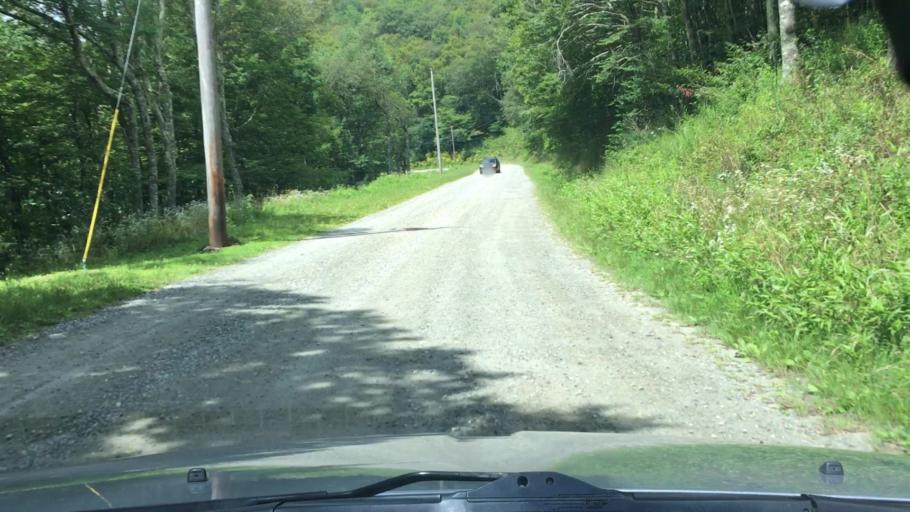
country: US
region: North Carolina
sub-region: Madison County
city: Mars Hill
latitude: 35.9809
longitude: -82.5003
